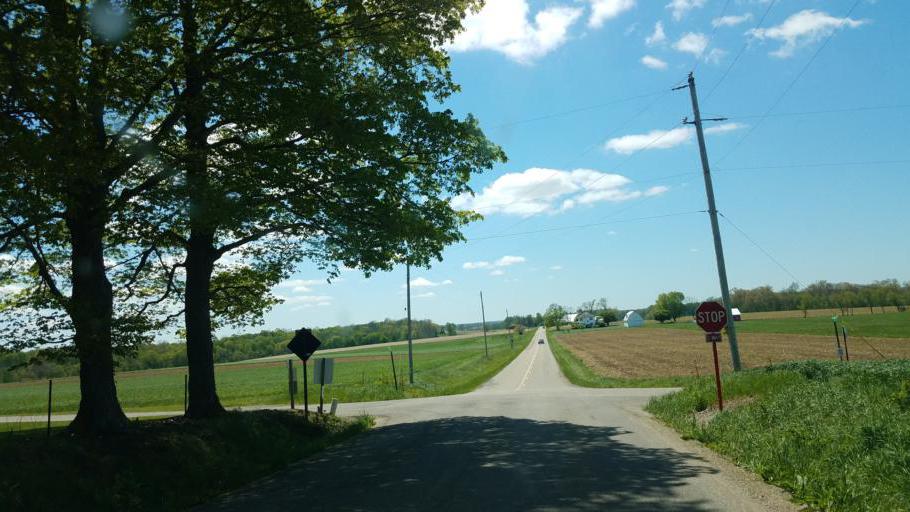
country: US
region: Ohio
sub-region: Knox County
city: Gambier
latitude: 40.4927
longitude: -82.3827
